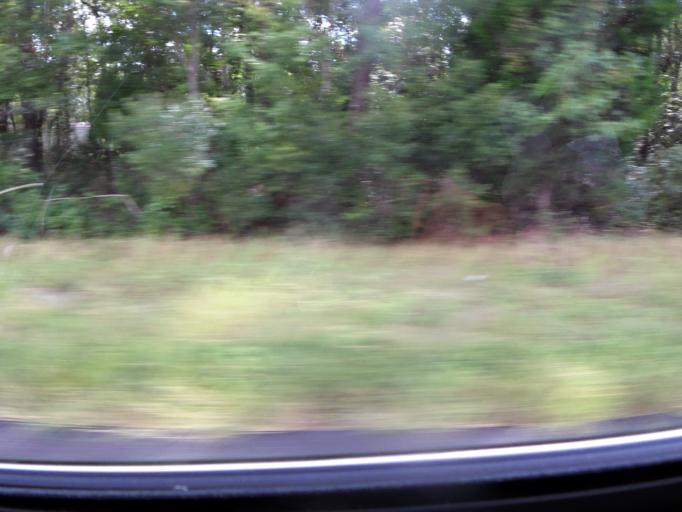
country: US
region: Georgia
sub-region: Glynn County
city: Dock Junction
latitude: 31.1803
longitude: -81.6338
